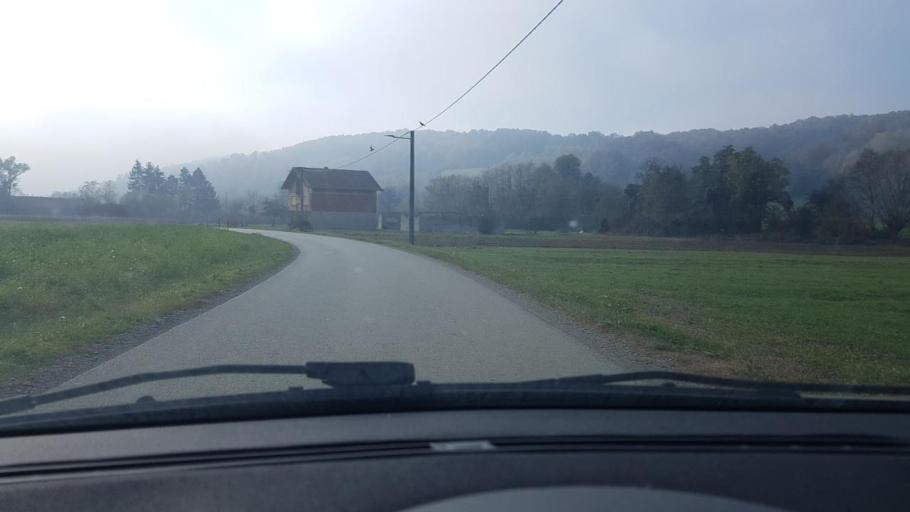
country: HR
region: Krapinsko-Zagorska
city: Zlatar
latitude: 46.1178
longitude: 16.0846
